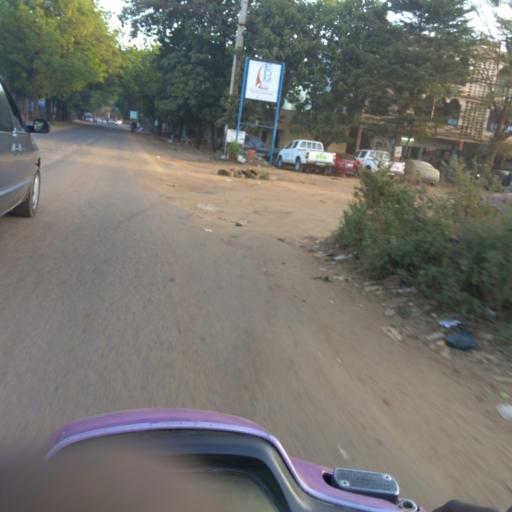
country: ML
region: Bamako
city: Bamako
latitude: 12.6517
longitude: -8.0136
